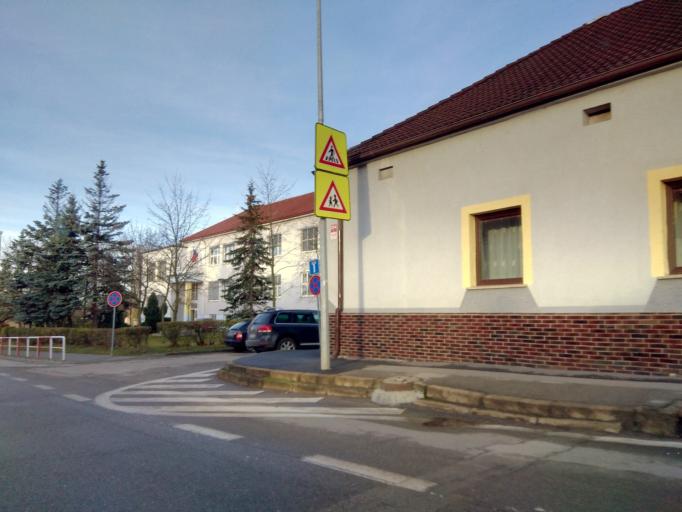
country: CZ
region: Jihocesky
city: Rudolfov
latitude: 48.9850
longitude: 14.5133
